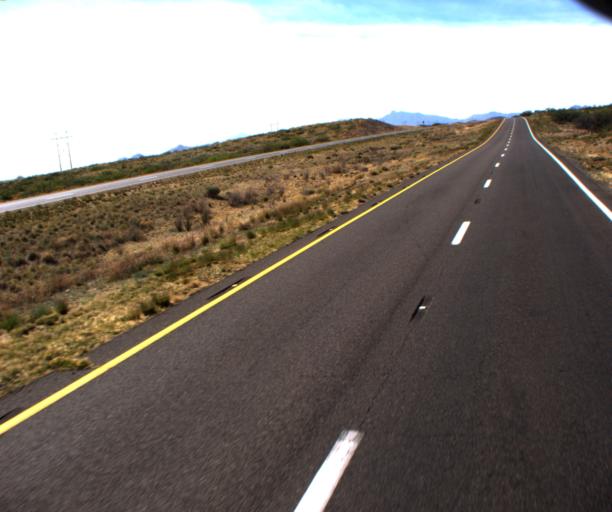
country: US
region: Arizona
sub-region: Graham County
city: Swift Trail Junction
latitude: 32.5079
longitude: -109.6743
